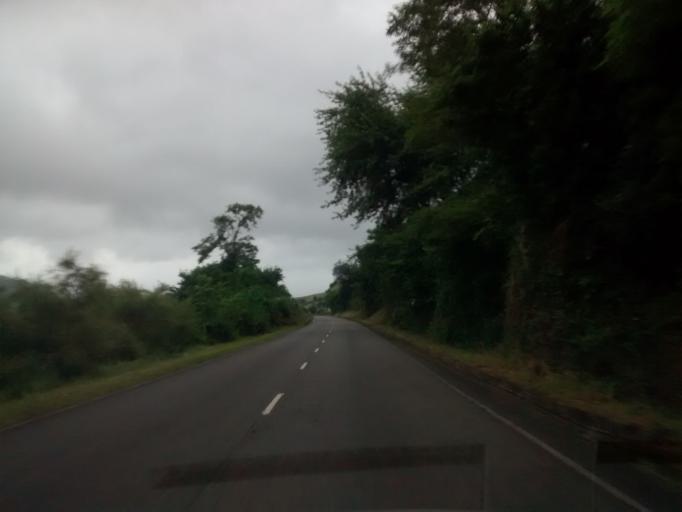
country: ES
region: Asturias
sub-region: Province of Asturias
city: Villaviciosa
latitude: 43.5052
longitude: -5.4238
